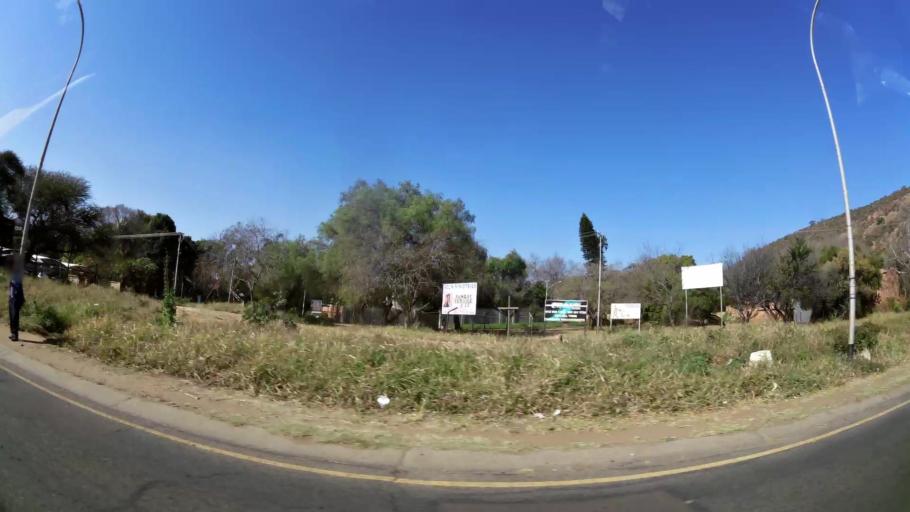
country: ZA
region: Gauteng
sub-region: City of Tshwane Metropolitan Municipality
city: Pretoria
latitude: -25.6861
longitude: 28.1927
